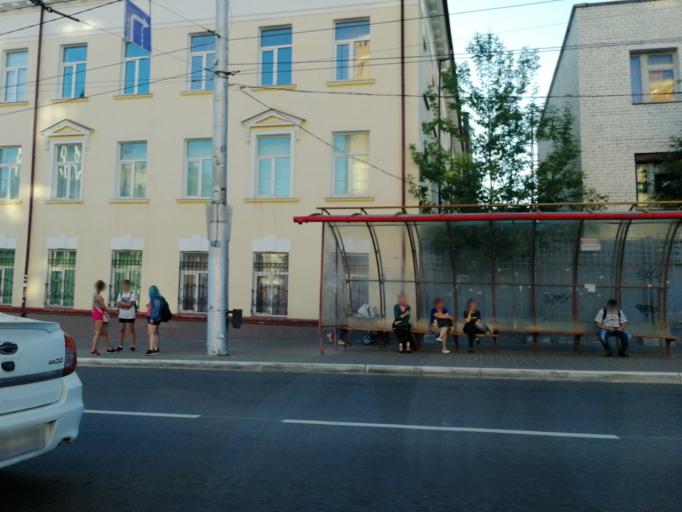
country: RU
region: Kaluga
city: Kaluga
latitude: 54.5140
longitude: 36.2395
